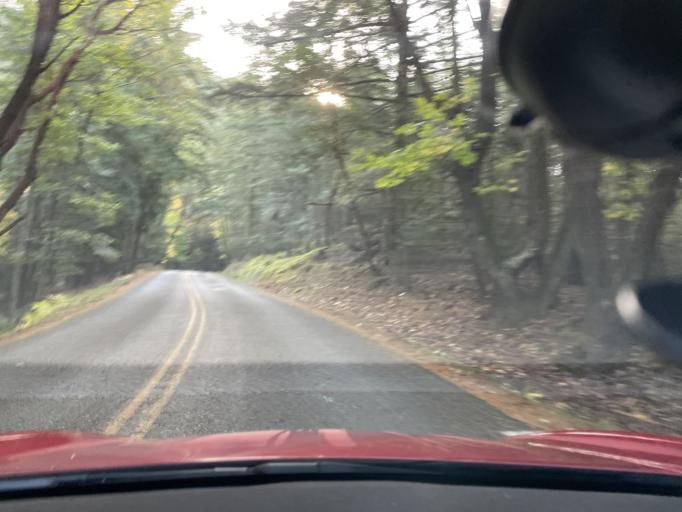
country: US
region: Washington
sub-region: San Juan County
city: Friday Harbor
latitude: 48.5193
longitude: -123.1432
